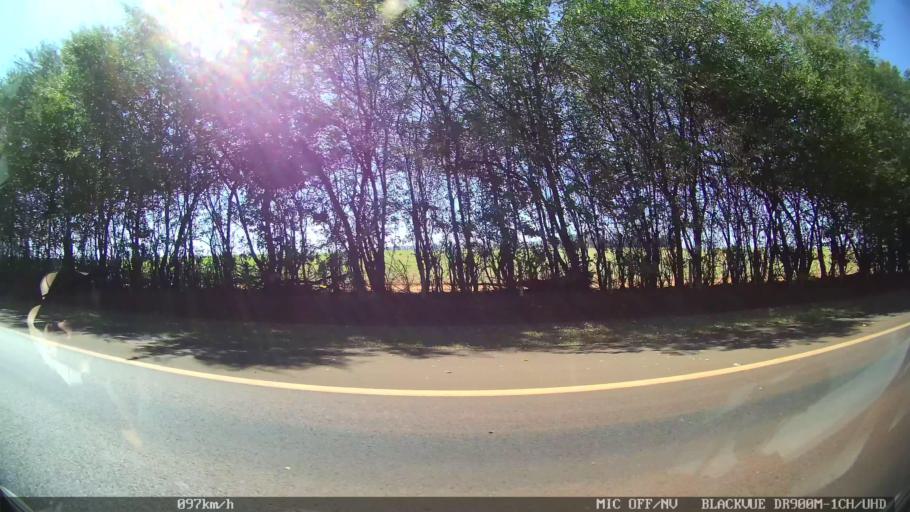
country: BR
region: Sao Paulo
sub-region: Batatais
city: Batatais
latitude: -20.7422
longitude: -47.5311
